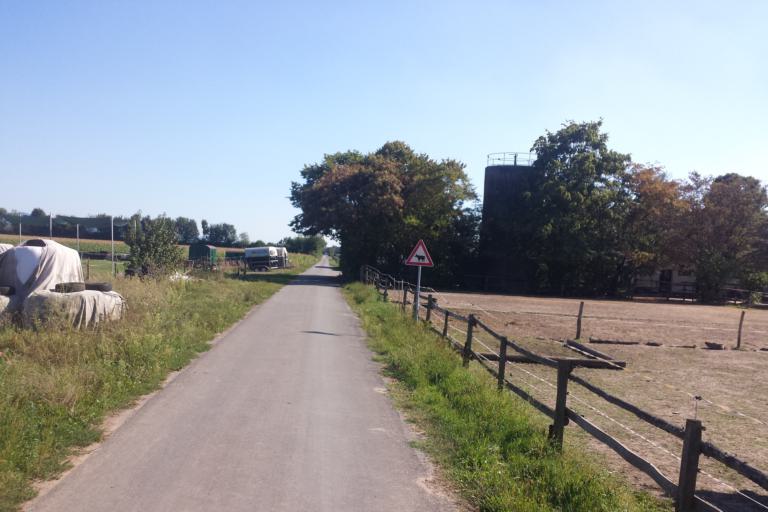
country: DE
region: Hesse
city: Viernheim
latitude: 49.5760
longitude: 8.5955
